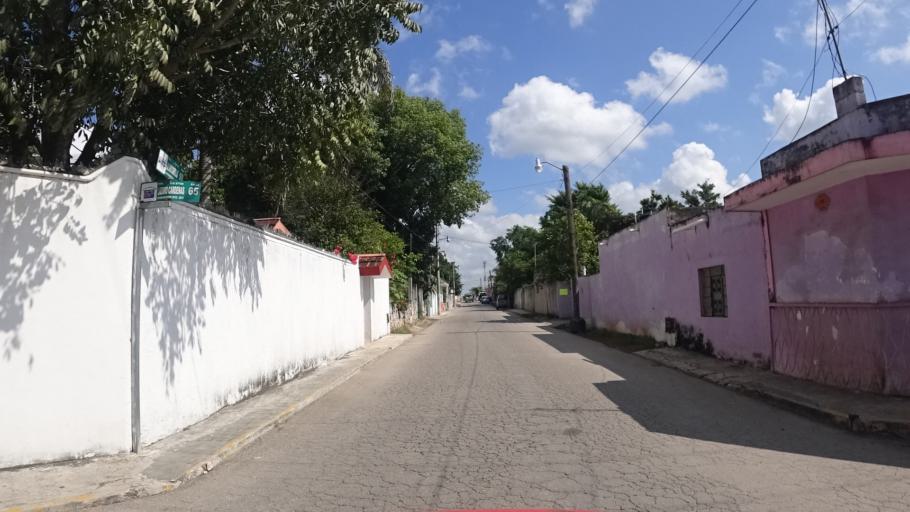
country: MX
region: Yucatan
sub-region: Tizimin
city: Tizimin
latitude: 21.1358
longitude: -88.1537
